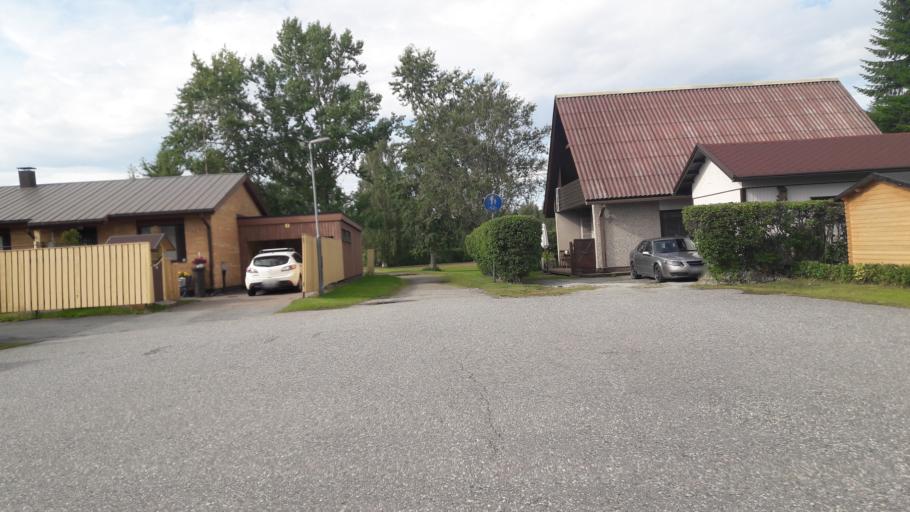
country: FI
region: North Karelia
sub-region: Joensuu
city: Joensuu
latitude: 62.5782
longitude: 29.8126
